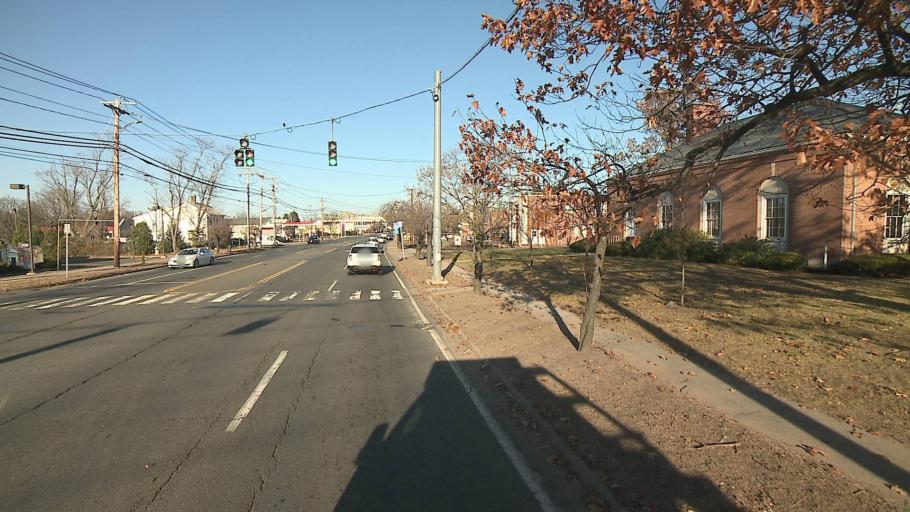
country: US
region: Connecticut
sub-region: New Haven County
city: North Haven
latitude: 41.3919
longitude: -72.8589
